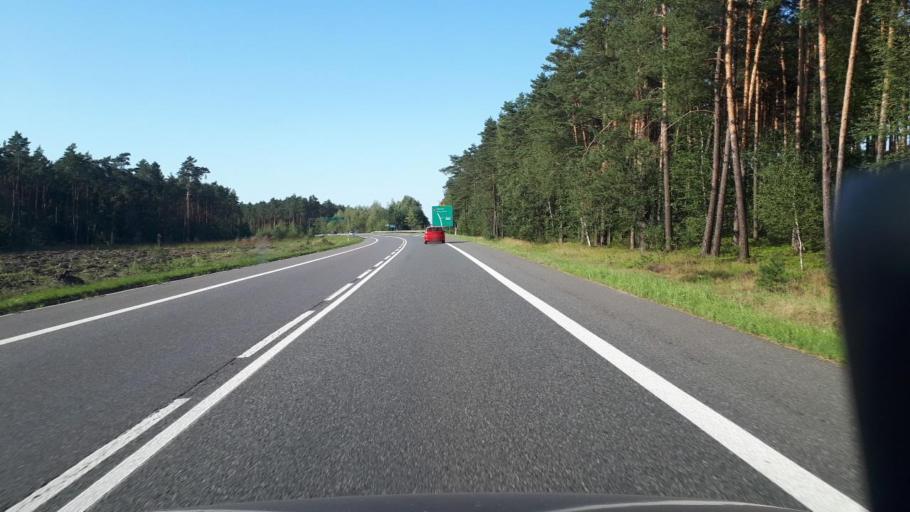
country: PL
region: Silesian Voivodeship
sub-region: Powiat lubliniecki
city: Lubliniec
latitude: 50.6405
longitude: 18.6856
